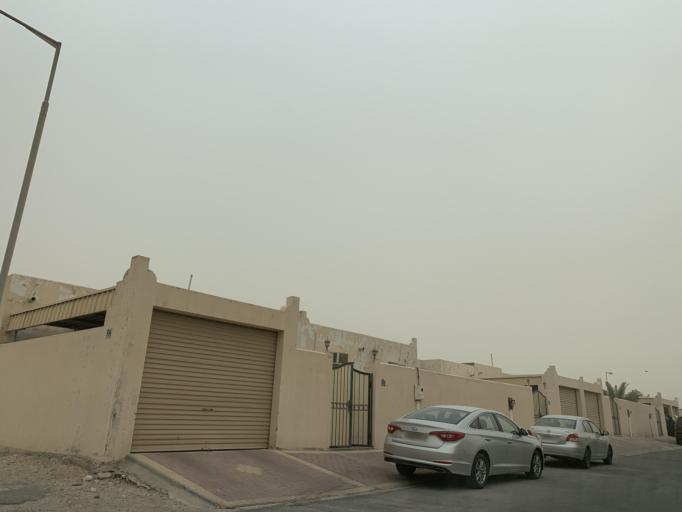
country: BH
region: Central Governorate
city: Madinat Hamad
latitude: 26.1322
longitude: 50.5246
